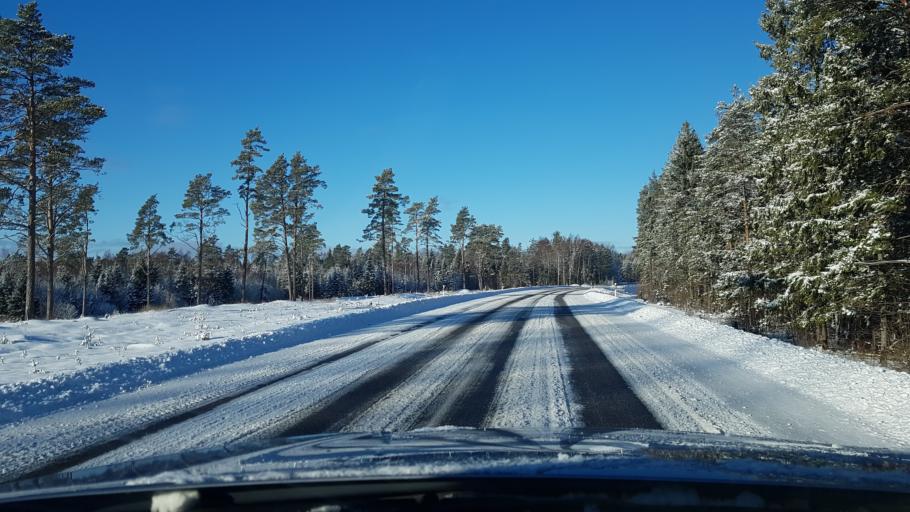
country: EE
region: Hiiumaa
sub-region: Kaerdla linn
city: Kardla
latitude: 58.9694
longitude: 22.7699
